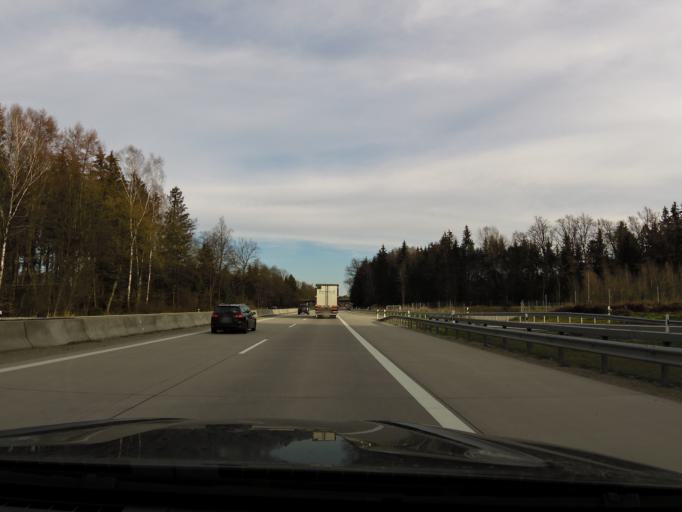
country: DE
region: Bavaria
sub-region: Upper Bavaria
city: Raubling
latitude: 47.7830
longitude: 12.0921
